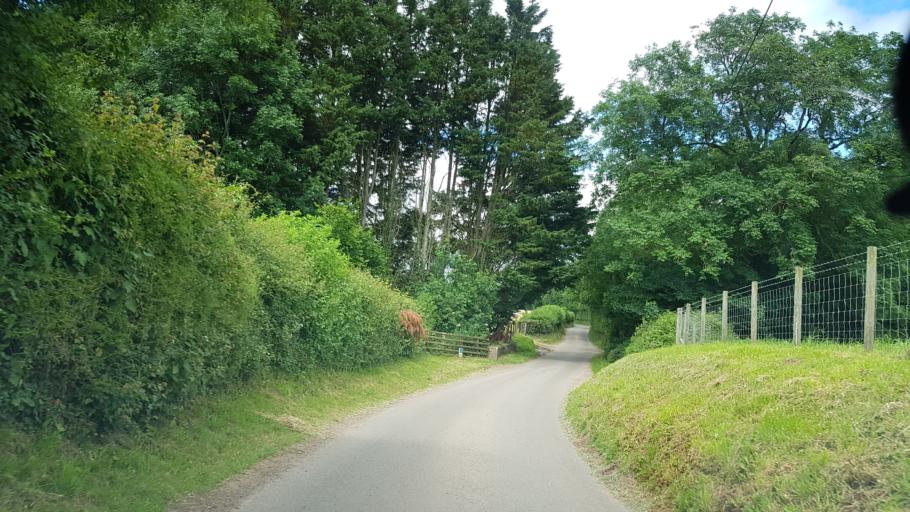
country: GB
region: Wales
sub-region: Monmouthshire
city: Llanarth
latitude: 51.8241
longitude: -2.8704
